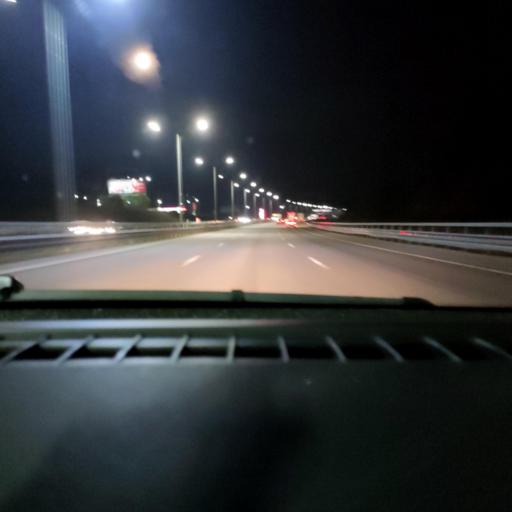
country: RU
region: Voronezj
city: Ramon'
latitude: 51.8279
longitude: 39.2461
